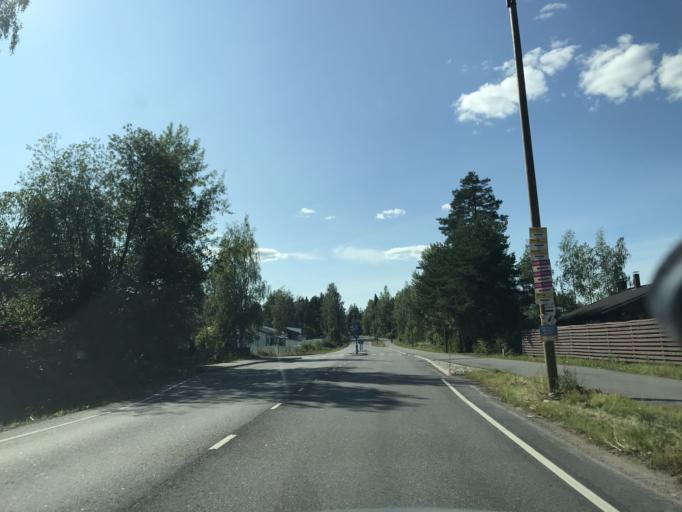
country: FI
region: Uusimaa
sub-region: Helsinki
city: Nurmijaervi
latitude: 60.3829
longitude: 24.6919
